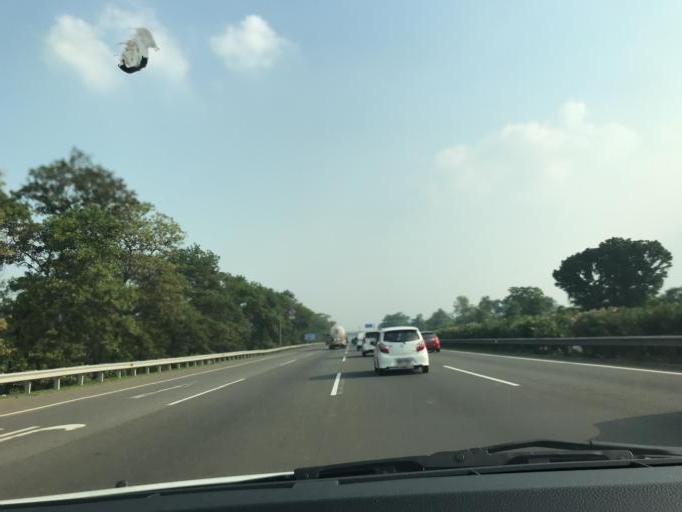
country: ID
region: West Java
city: Citeureup
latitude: -6.4641
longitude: 106.8835
